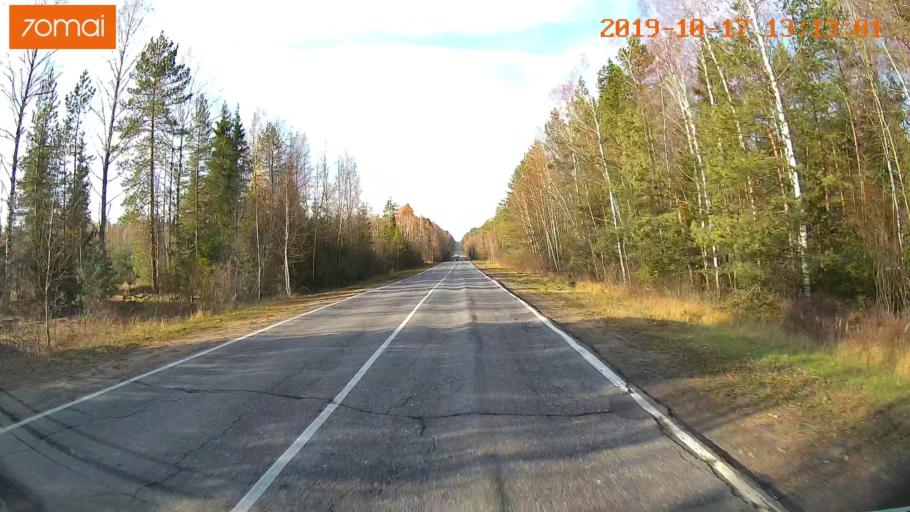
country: RU
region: Rjazan
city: Gus'-Zheleznyy
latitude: 55.0415
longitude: 41.2001
